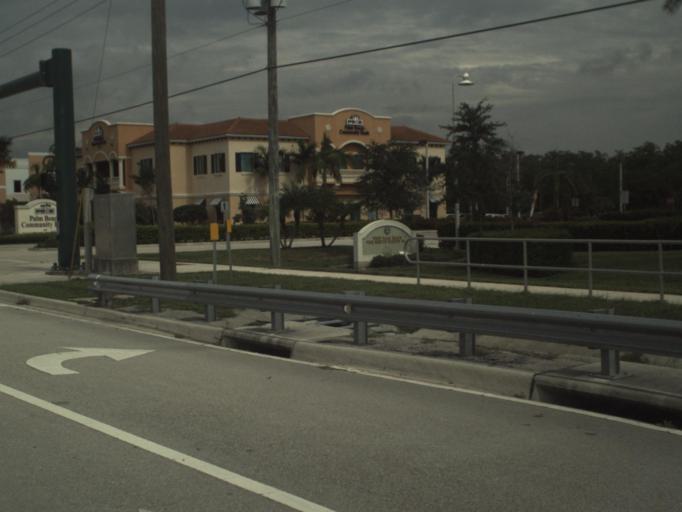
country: US
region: Florida
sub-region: Palm Beach County
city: Plantation Mobile Home Park
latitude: 26.7087
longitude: -80.1696
